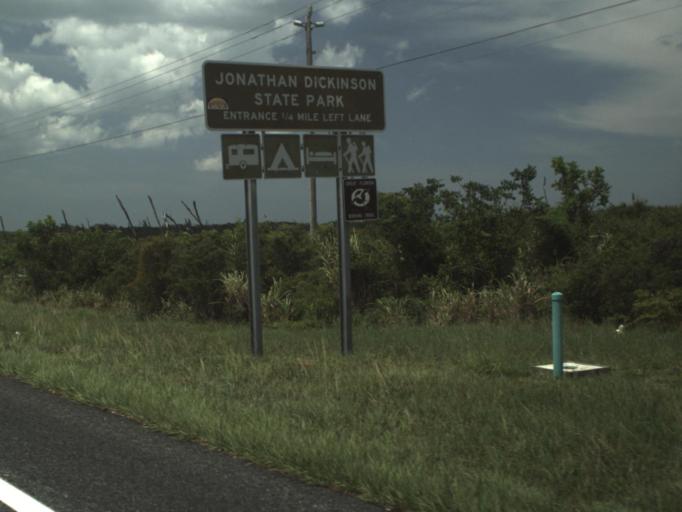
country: US
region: Florida
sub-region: Palm Beach County
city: Tequesta
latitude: 27.0005
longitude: -80.0987
